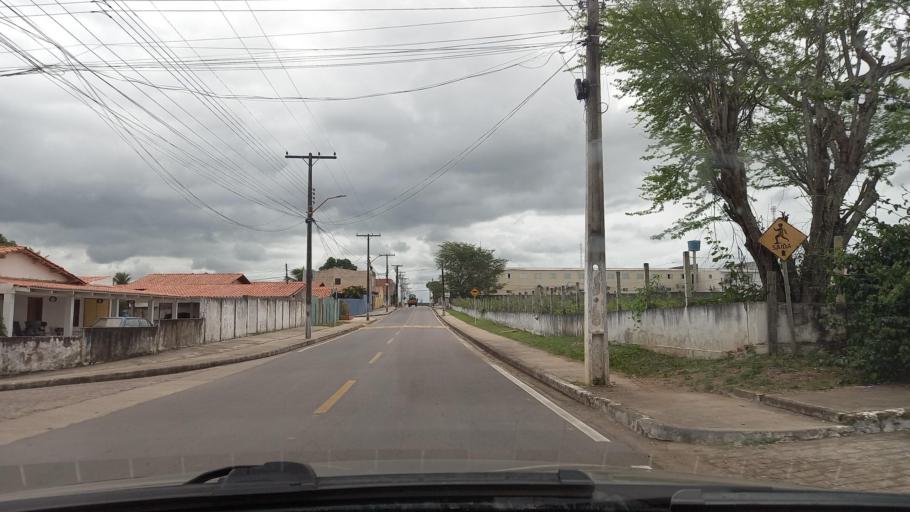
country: BR
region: Sergipe
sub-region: Caninde De Sao Francisco
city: Caninde de Sao Francisco
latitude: -9.6108
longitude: -37.7635
